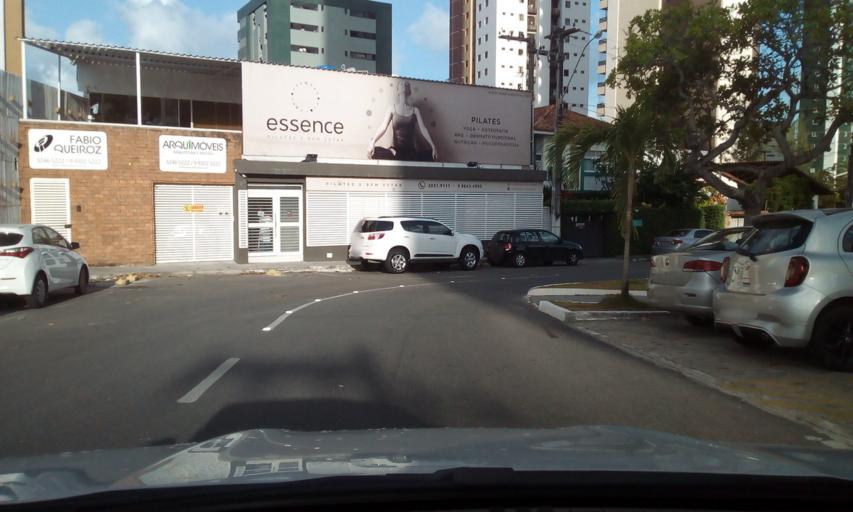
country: BR
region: Paraiba
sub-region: Joao Pessoa
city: Joao Pessoa
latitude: -7.1210
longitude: -34.8339
